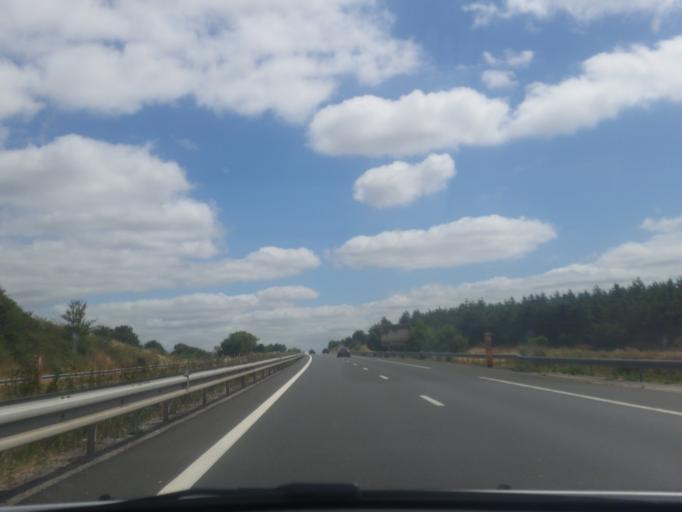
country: FR
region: Pays de la Loire
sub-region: Departement de Maine-et-Loire
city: Champtoce-sur-Loire
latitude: 47.4356
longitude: -0.8565
